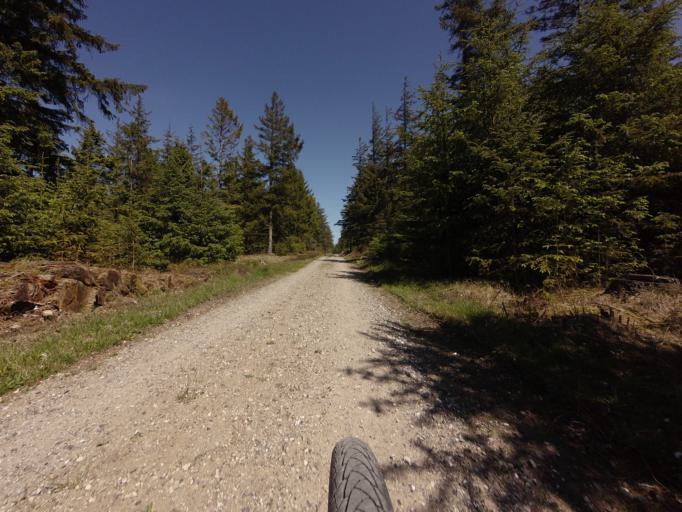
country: DK
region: North Denmark
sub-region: Jammerbugt Kommune
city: Pandrup
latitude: 57.2287
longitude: 9.5819
